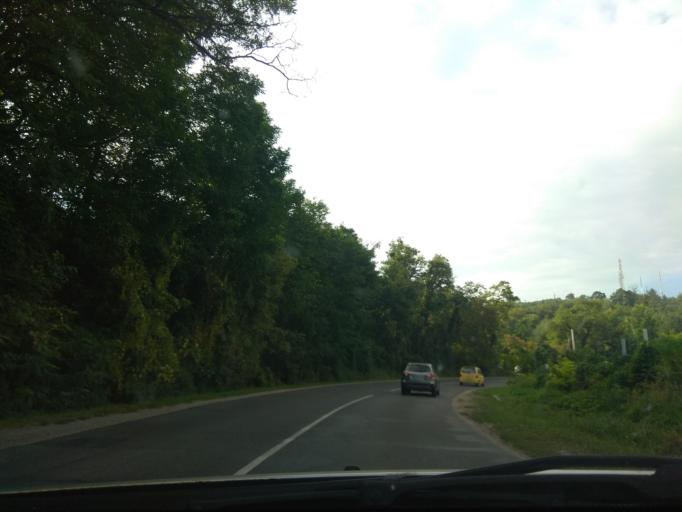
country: HU
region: Borsod-Abauj-Zemplen
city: Miskolc
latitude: 48.0871
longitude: 20.7420
